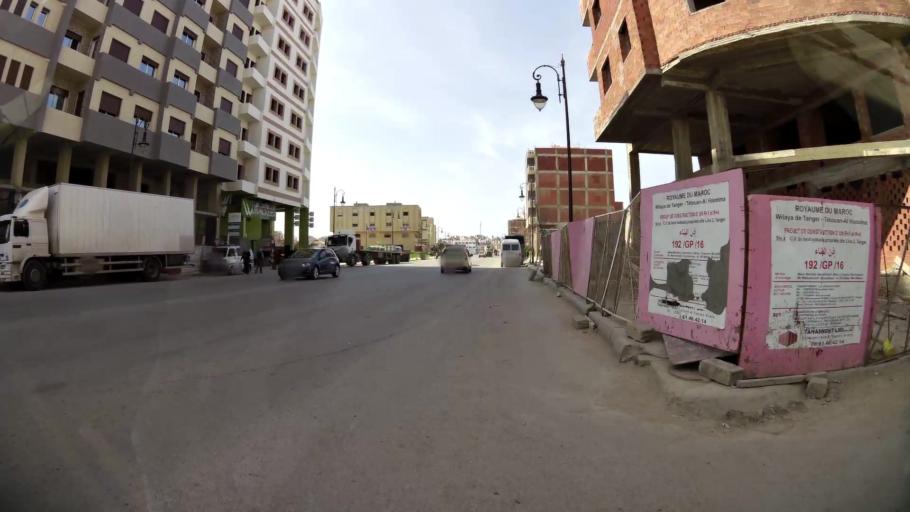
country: MA
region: Tanger-Tetouan
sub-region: Tanger-Assilah
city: Tangier
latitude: 35.7261
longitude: -5.8042
